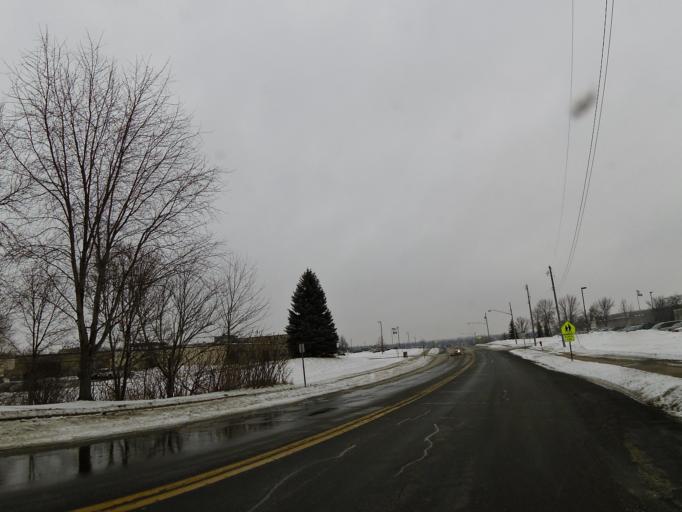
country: US
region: Minnesota
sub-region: Scott County
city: Prior Lake
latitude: 44.7213
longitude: -93.4039
